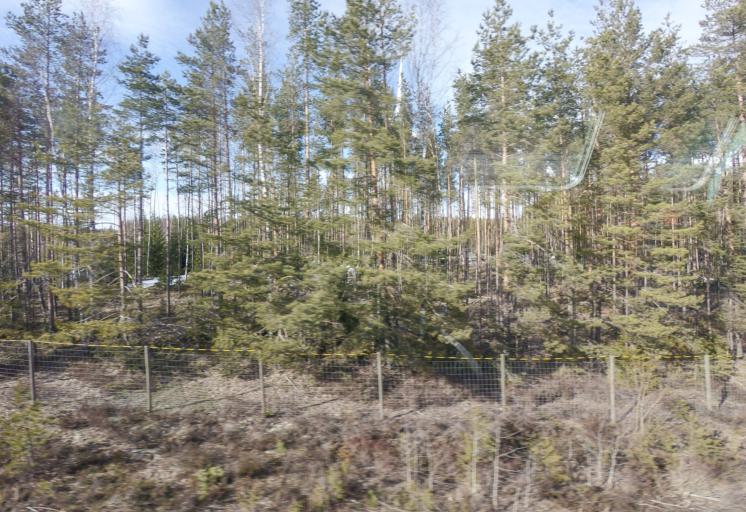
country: FI
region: South Karelia
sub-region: Lappeenranta
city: Joutseno
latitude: 61.1006
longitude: 28.3978
